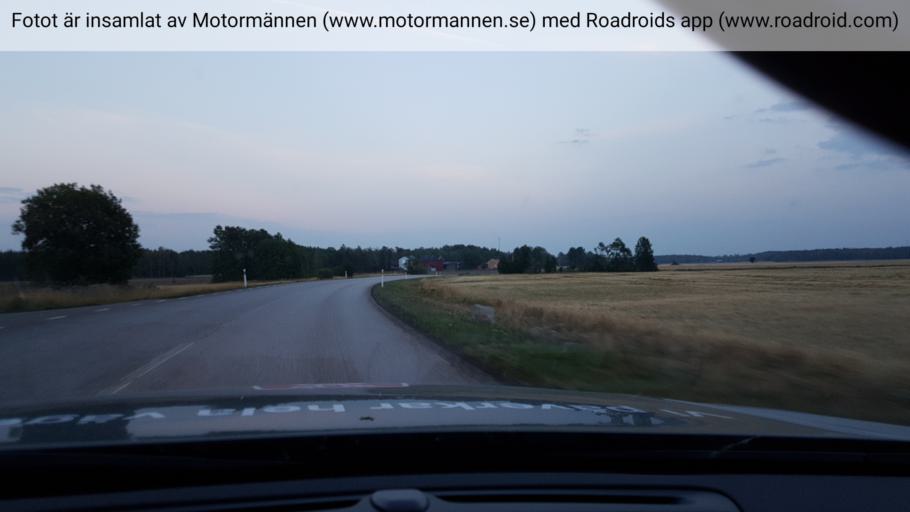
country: SE
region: Vaestmanland
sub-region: Sala Kommun
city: Sala
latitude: 59.8341
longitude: 16.7146
